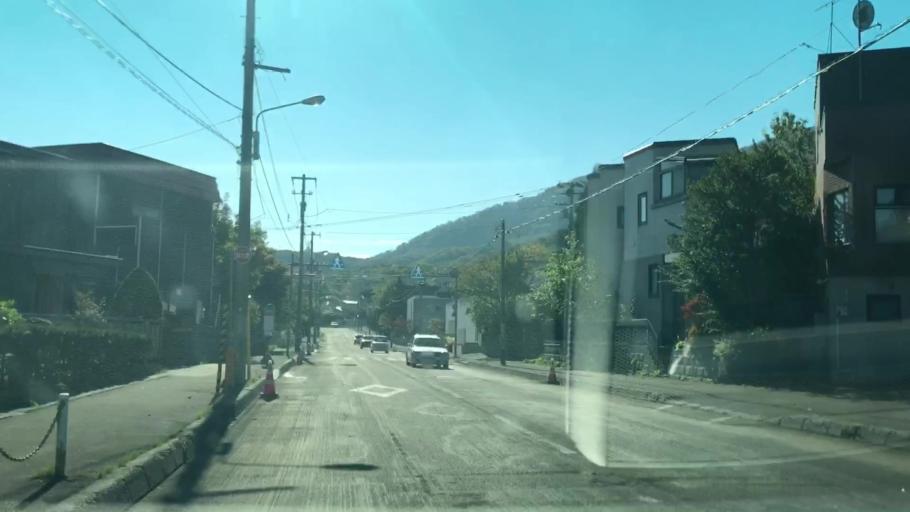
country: JP
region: Hokkaido
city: Sapporo
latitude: 43.0404
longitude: 141.3203
